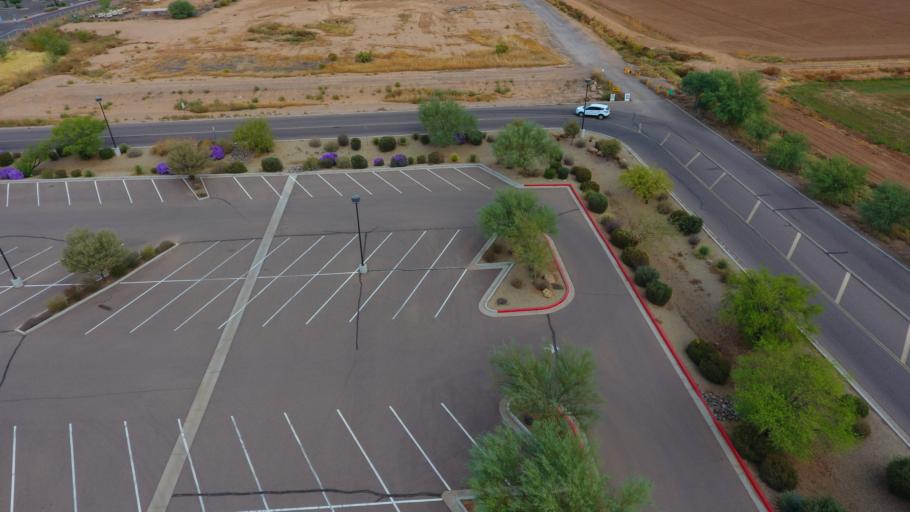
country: US
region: Arizona
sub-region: Maricopa County
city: Scottsdale
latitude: 33.5122
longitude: -111.8789
